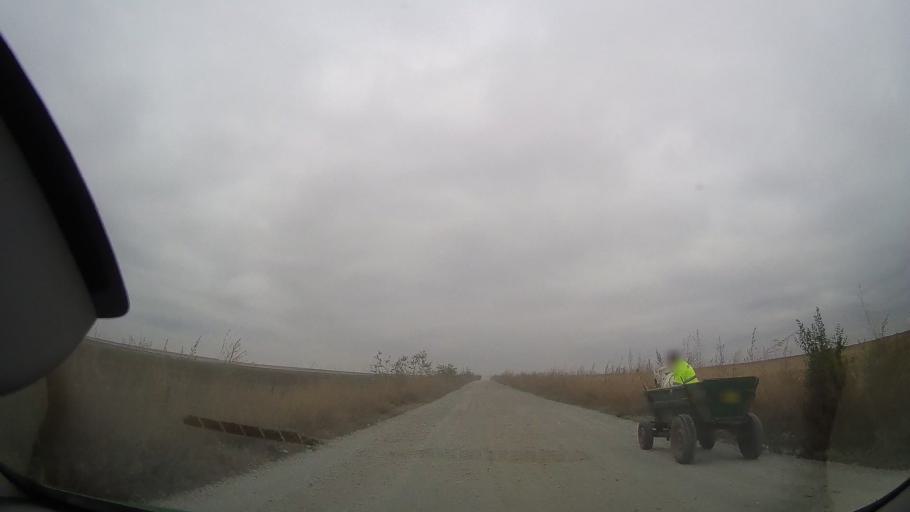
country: RO
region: Ialomita
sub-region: Comuna Grivita
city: Grivita
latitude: 44.7446
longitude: 27.2697
